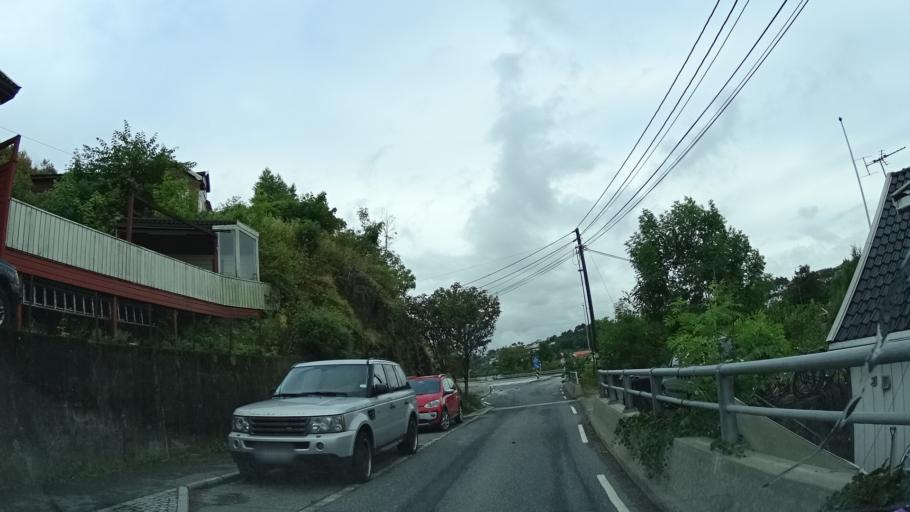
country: NO
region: Aust-Agder
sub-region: Arendal
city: Arendal
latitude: 58.4454
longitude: 8.7466
